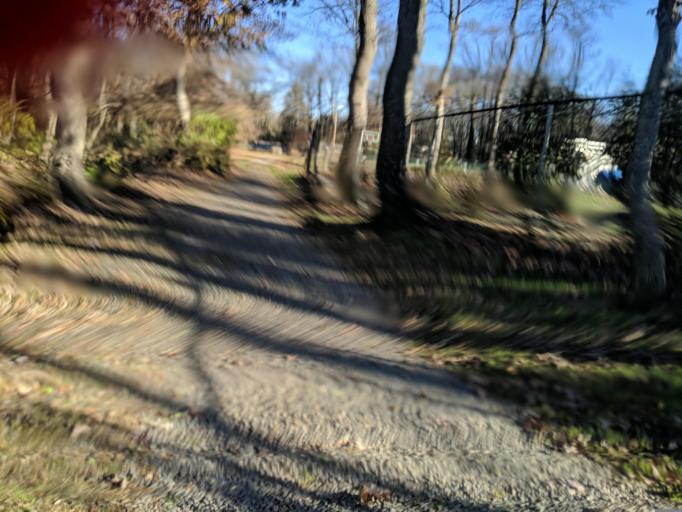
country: US
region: Virginia
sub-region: Fairfax County
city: Vienna
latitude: 38.8909
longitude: -77.2544
